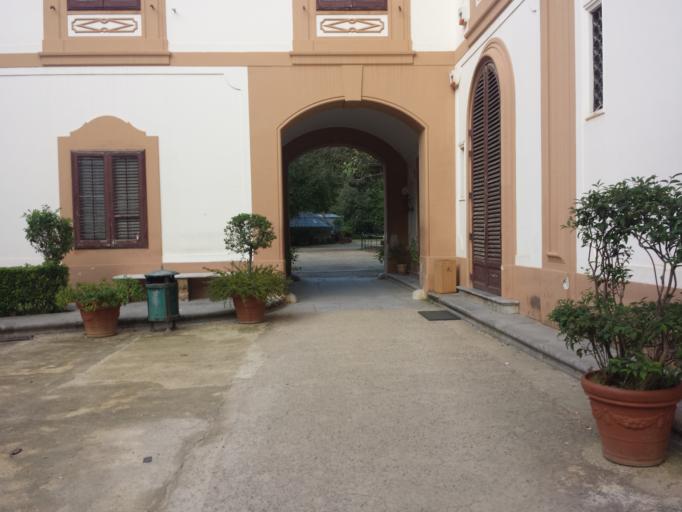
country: IT
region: Sicily
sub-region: Palermo
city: Palermo
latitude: 38.1293
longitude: 13.3462
